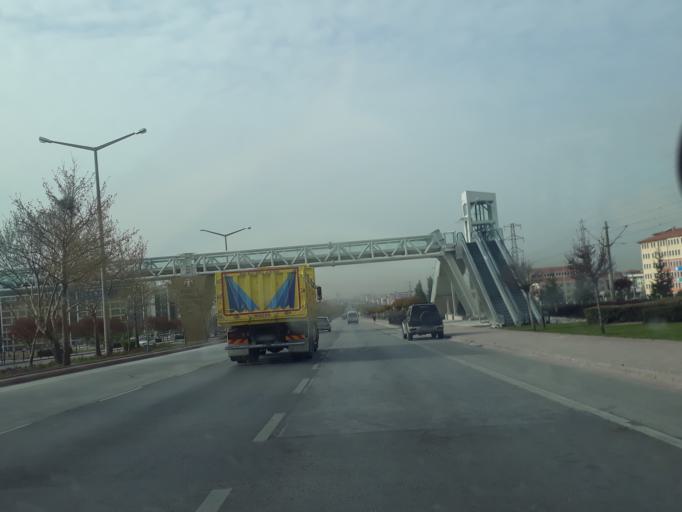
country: TR
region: Konya
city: Asagipinarbasi
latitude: 37.9877
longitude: 32.5178
